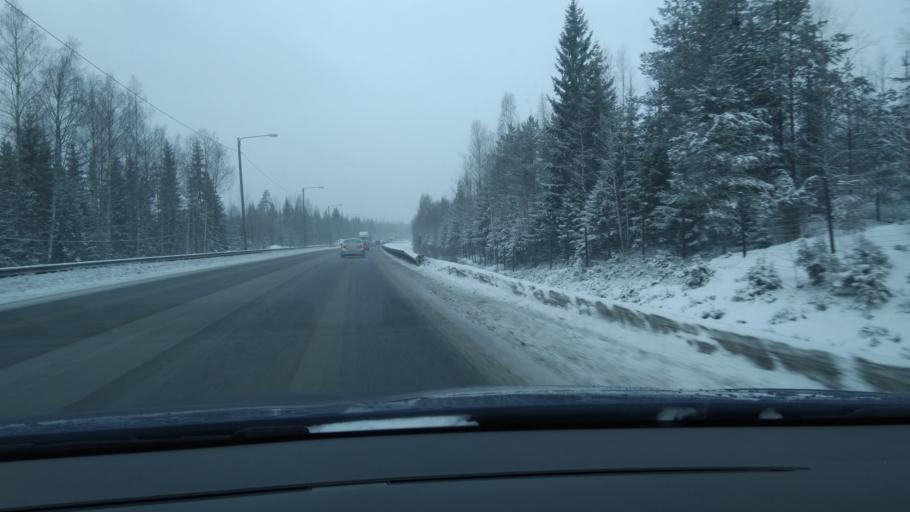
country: FI
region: Pirkanmaa
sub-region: Tampere
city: Kangasala
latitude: 61.5395
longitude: 24.0178
